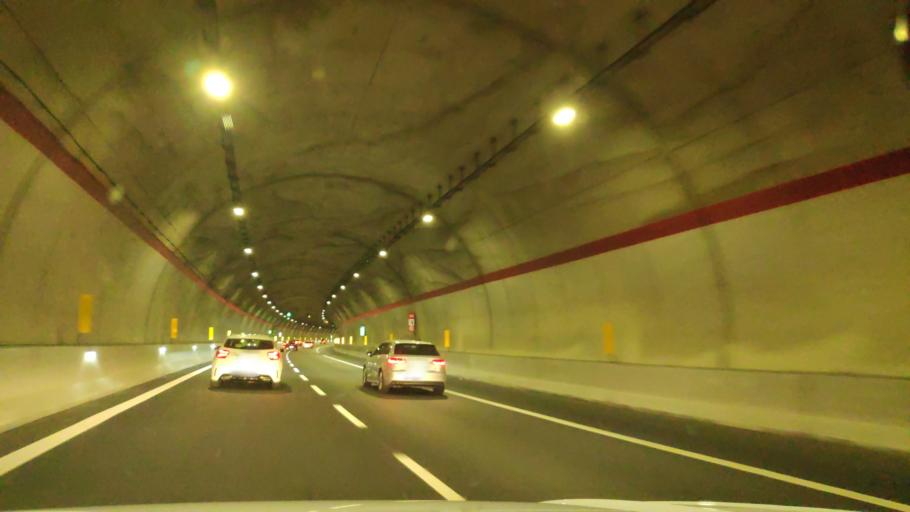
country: IT
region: Calabria
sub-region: Provincia di Cosenza
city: Mormanno
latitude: 39.8866
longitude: 15.9828
